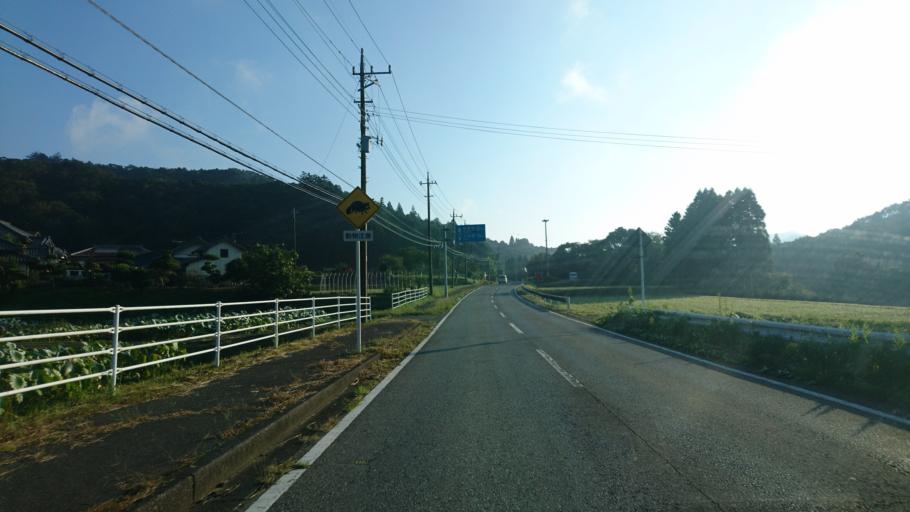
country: JP
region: Chiba
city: Kawaguchi
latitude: 35.1890
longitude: 140.0087
